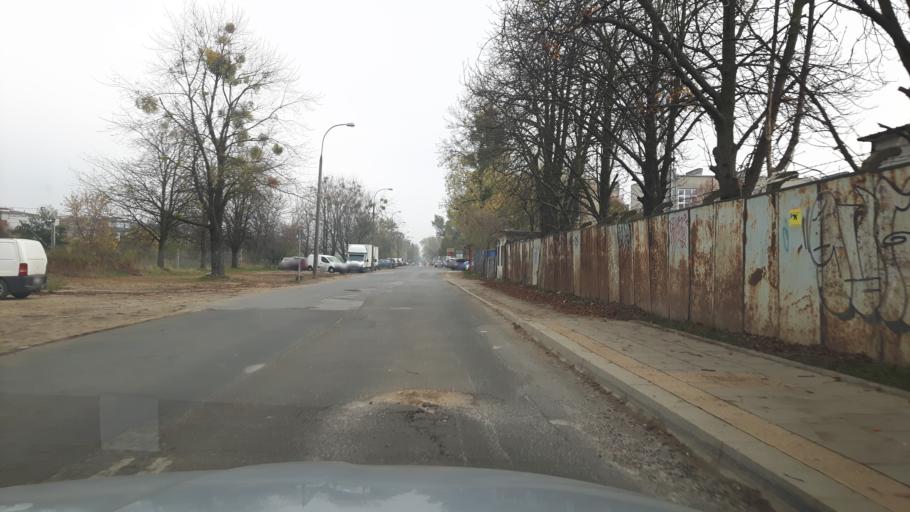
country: PL
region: Masovian Voivodeship
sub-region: Warszawa
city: Wlochy
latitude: 52.2004
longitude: 20.9490
